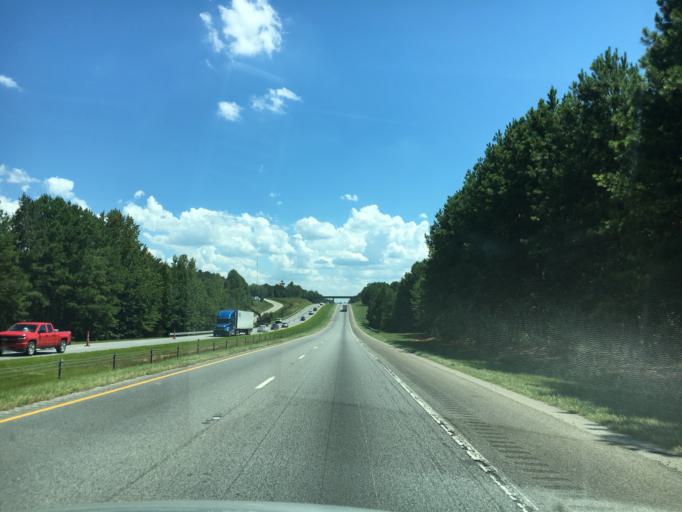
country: US
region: South Carolina
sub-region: Spartanburg County
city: Woodruff
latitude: 34.7095
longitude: -81.9426
